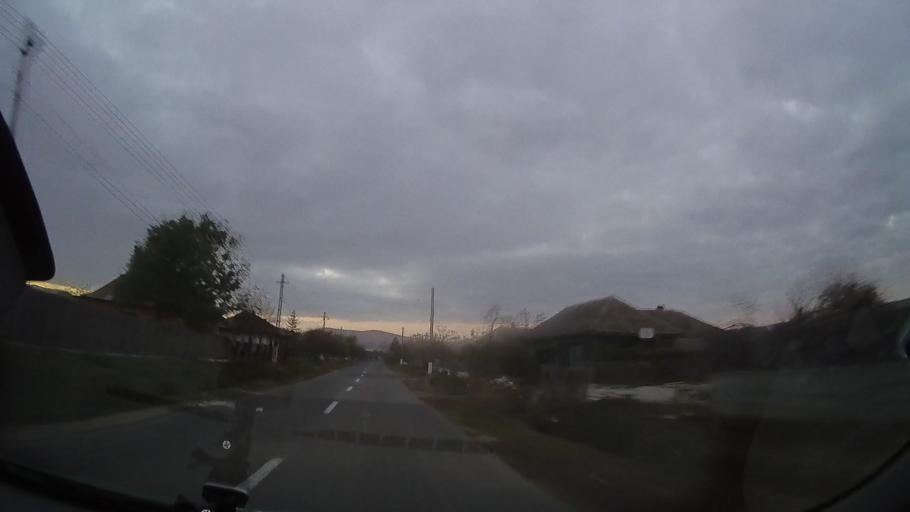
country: RO
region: Tulcea
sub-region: Comuna Mihai Bravu
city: Turda
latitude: 44.9767
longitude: 28.6202
